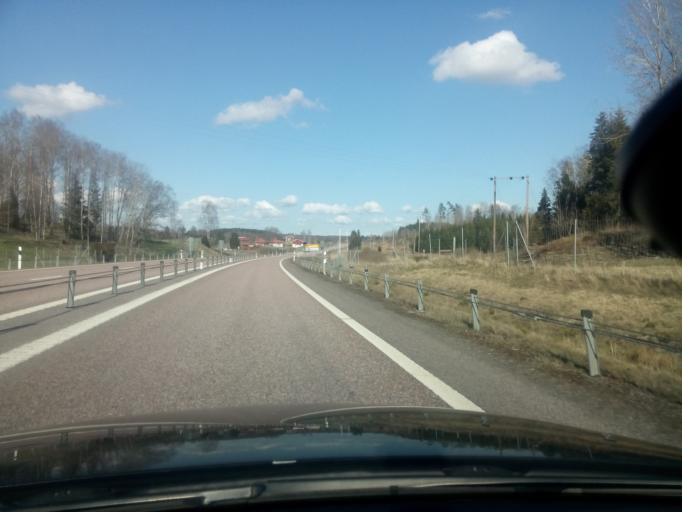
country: SE
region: Soedermanland
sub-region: Flens Kommun
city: Malmkoping
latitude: 59.1545
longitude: 16.7282
